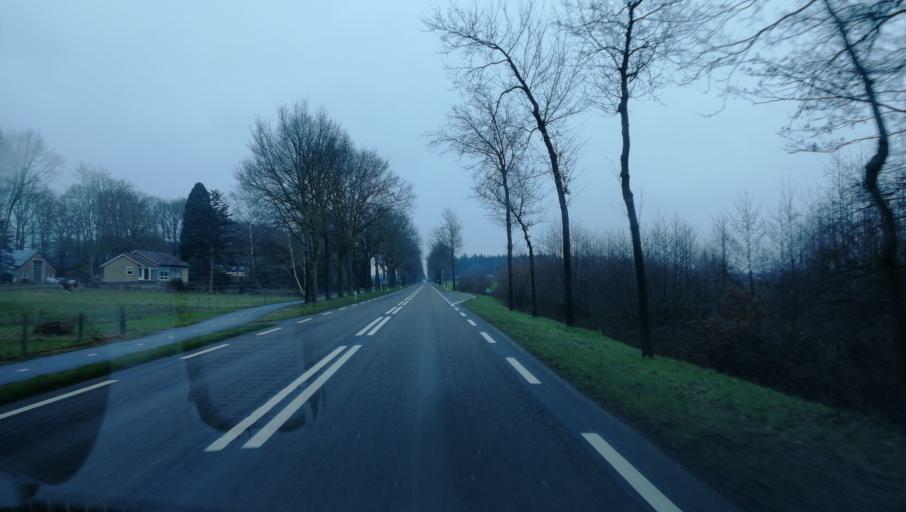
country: NL
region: Limburg
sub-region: Gemeente Beesel
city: Reuver
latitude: 51.3144
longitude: 6.0727
